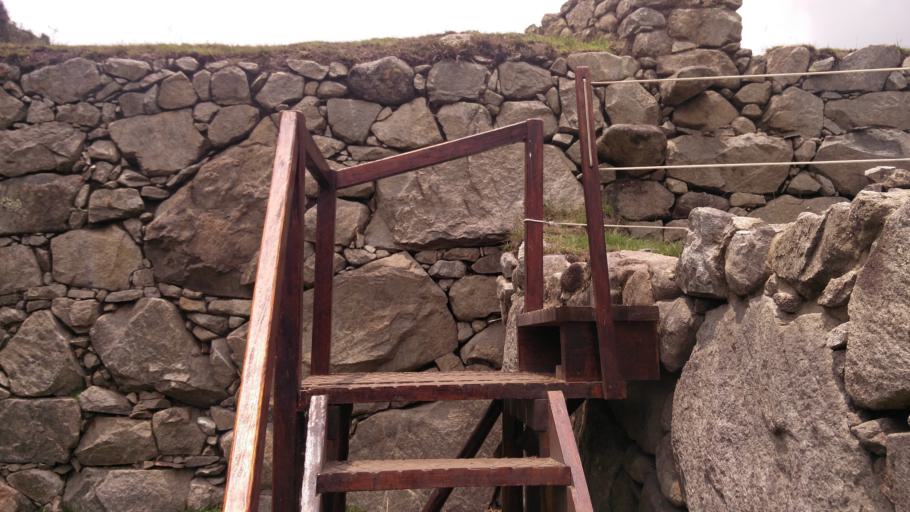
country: PE
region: Cusco
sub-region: Provincia de La Convencion
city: Santa Teresa
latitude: -13.1656
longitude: -72.5445
